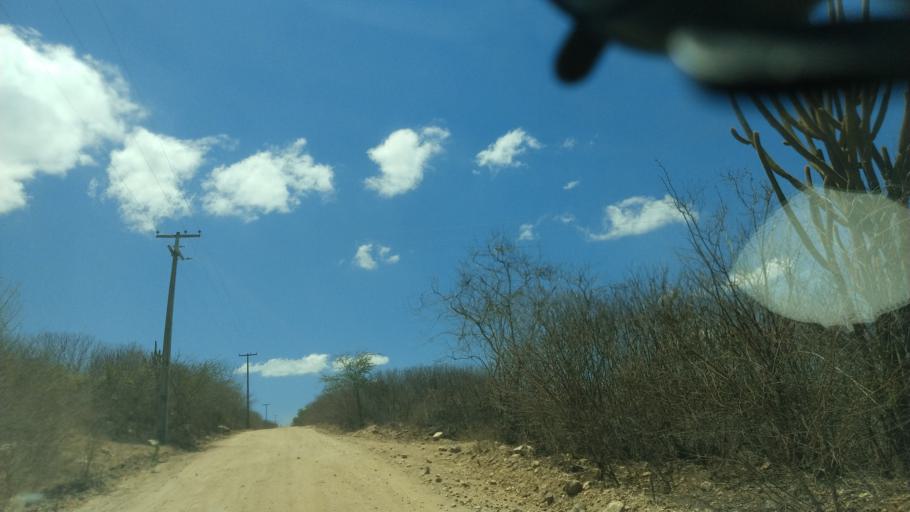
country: BR
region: Rio Grande do Norte
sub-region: Cerro Cora
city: Cerro Cora
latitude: -6.0139
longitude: -36.3270
